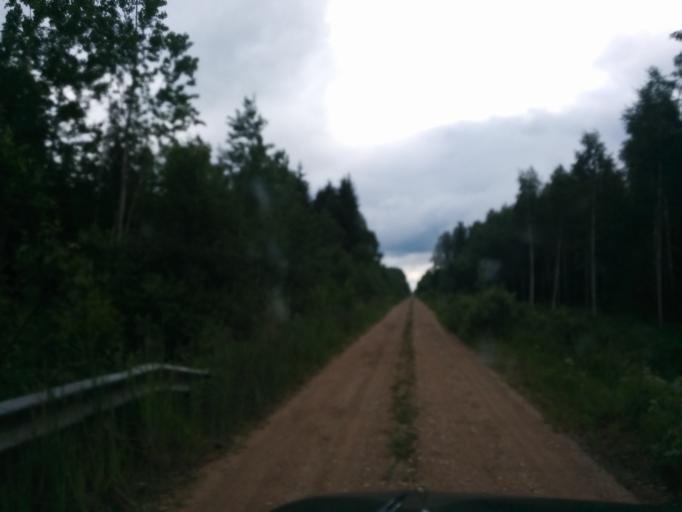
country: LV
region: Vilaka
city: Vilaka
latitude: 57.3925
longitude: 27.5869
